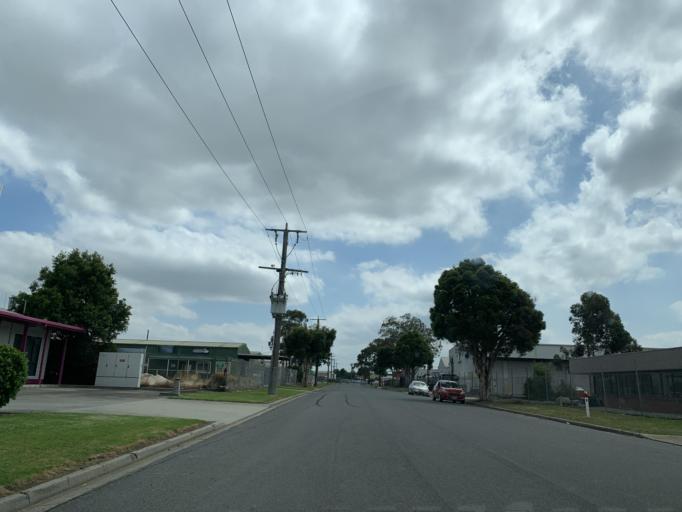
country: AU
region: Victoria
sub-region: Latrobe
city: Traralgon
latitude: -38.1910
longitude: 146.5663
